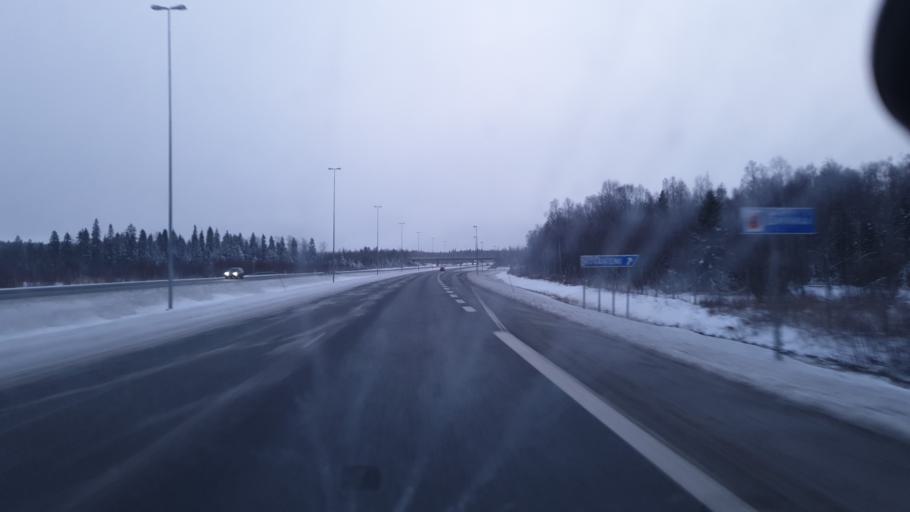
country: FI
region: Lapland
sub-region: Kemi-Tornio
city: Keminmaa
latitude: 65.8212
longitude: 24.4803
